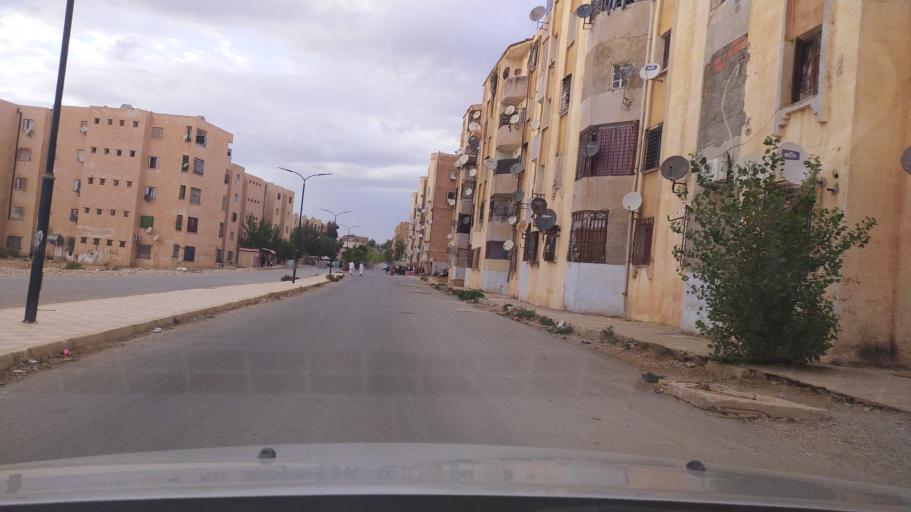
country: DZ
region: Tiaret
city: Frenda
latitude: 35.0552
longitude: 1.0622
